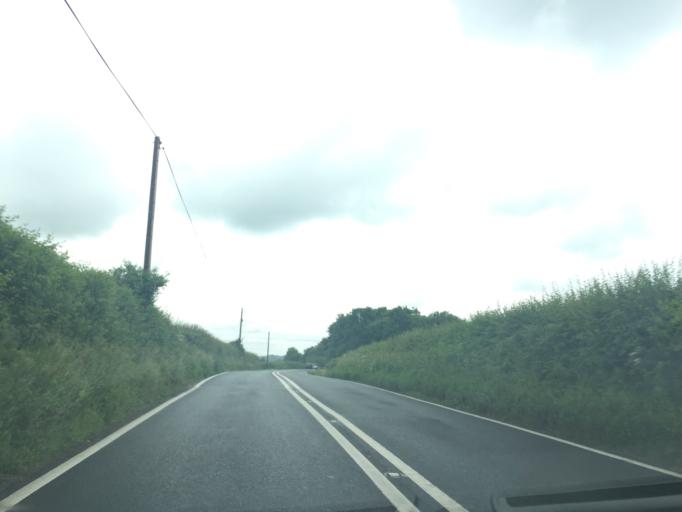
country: GB
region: England
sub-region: Dorset
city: Lytchett Matravers
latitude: 50.7878
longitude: -2.0846
